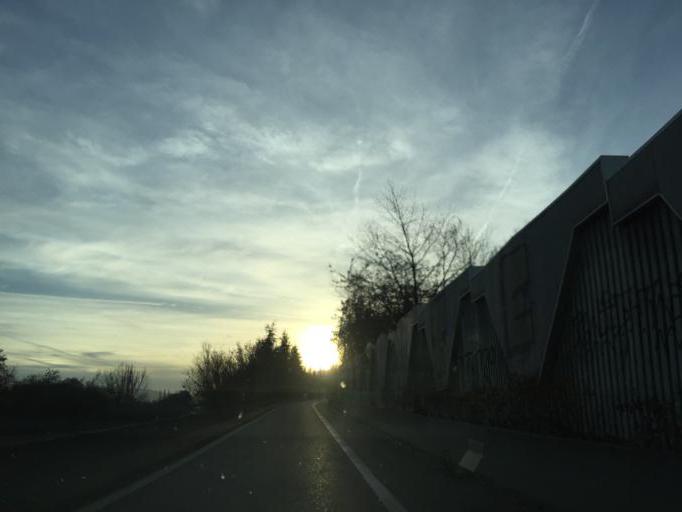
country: FR
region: Rhone-Alpes
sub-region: Departement de la Loire
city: La Grand-Croix
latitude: 45.4961
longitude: 4.5565
